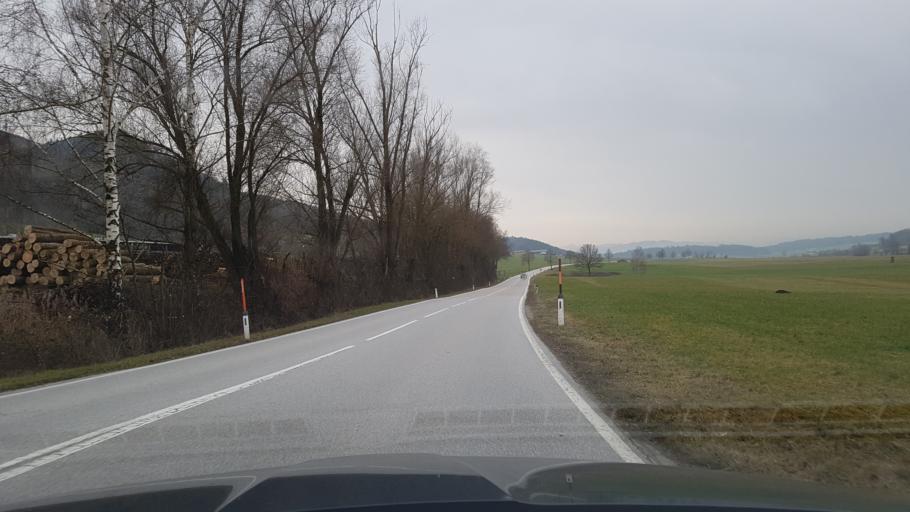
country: AT
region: Salzburg
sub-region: Politischer Bezirk Salzburg-Umgebung
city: Dorfbeuern
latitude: 48.0027
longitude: 13.0351
